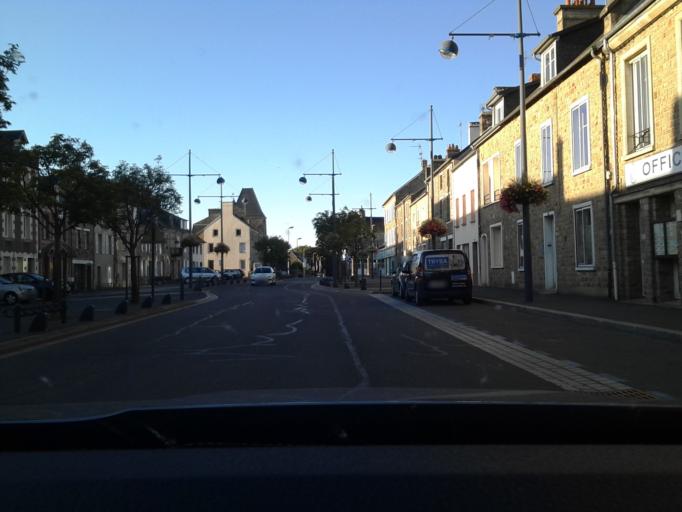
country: FR
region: Lower Normandy
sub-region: Departement de la Manche
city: La Haye-du-Puits
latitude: 49.2917
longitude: -1.5451
